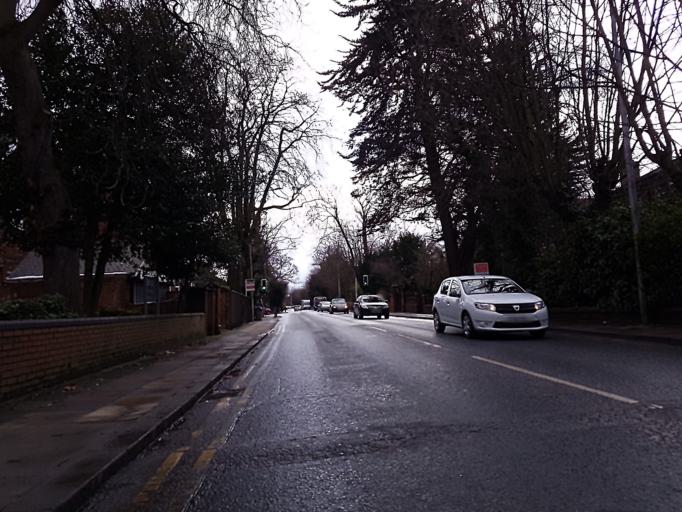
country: GB
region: England
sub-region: North East Lincolnshire
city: Grimbsy
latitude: 53.5604
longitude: -0.0922
